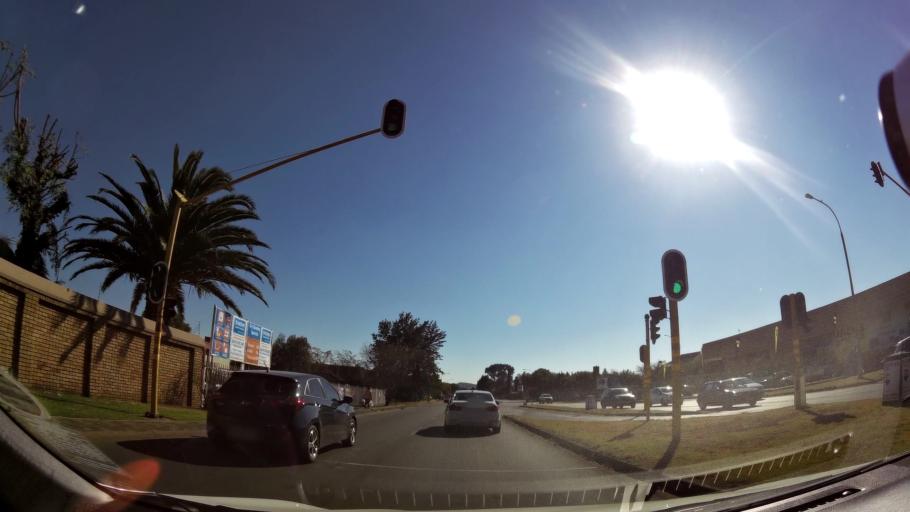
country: ZA
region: Gauteng
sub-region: Ekurhuleni Metropolitan Municipality
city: Germiston
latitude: -26.3149
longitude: 28.0963
